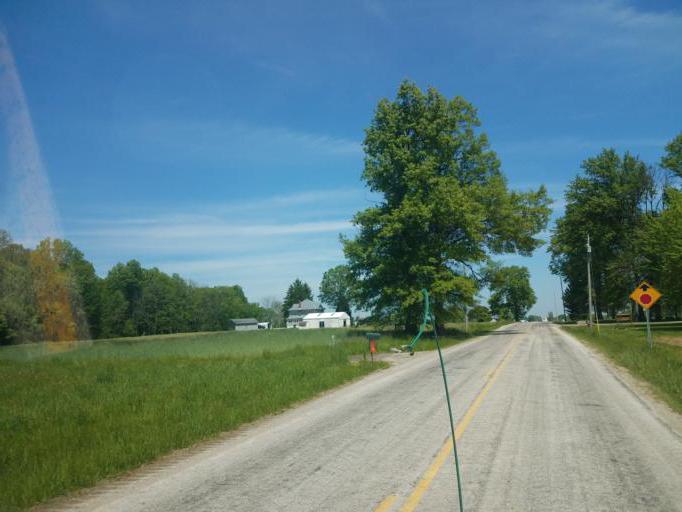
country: US
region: Ohio
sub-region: Ashland County
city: Ashland
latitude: 40.9213
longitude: -82.2433
